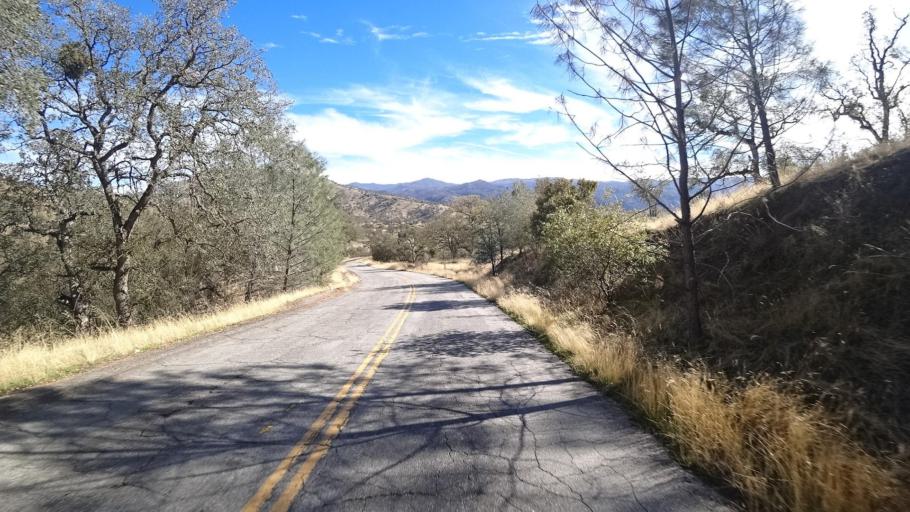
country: US
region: California
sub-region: Kern County
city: Alta Sierra
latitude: 35.6295
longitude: -118.7571
